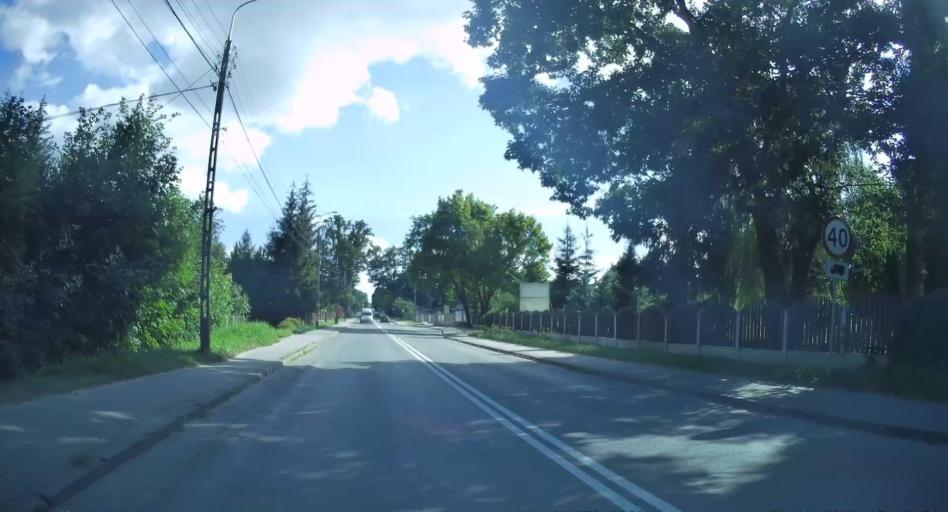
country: PL
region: Swietokrzyskie
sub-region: Powiat skarzyski
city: Suchedniow
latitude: 51.0446
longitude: 20.8376
